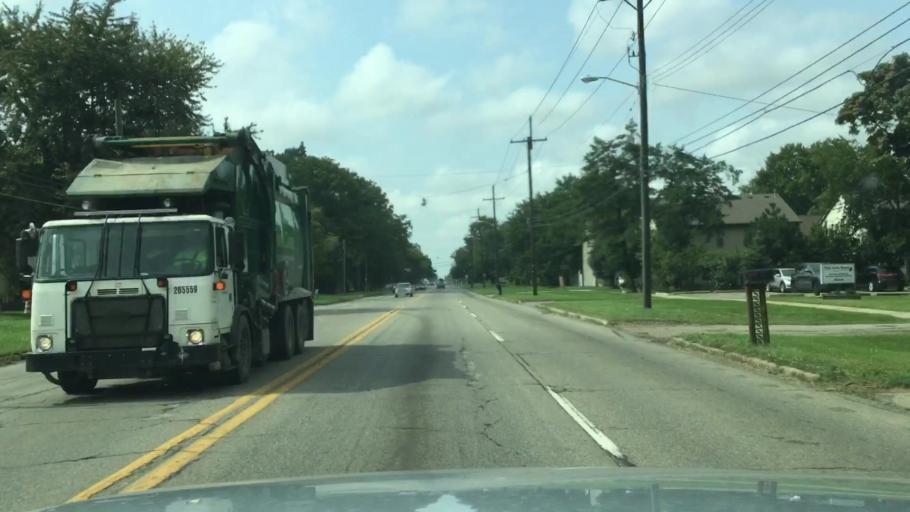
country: US
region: Michigan
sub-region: Wayne County
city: Wayne
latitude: 42.2669
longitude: -83.3764
